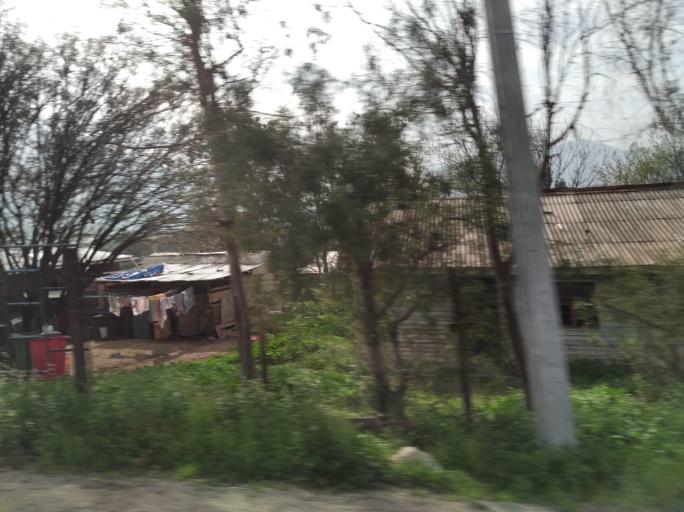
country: CL
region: Santiago Metropolitan
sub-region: Provincia de Chacabuco
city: Lampa
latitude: -33.2616
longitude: -70.8983
